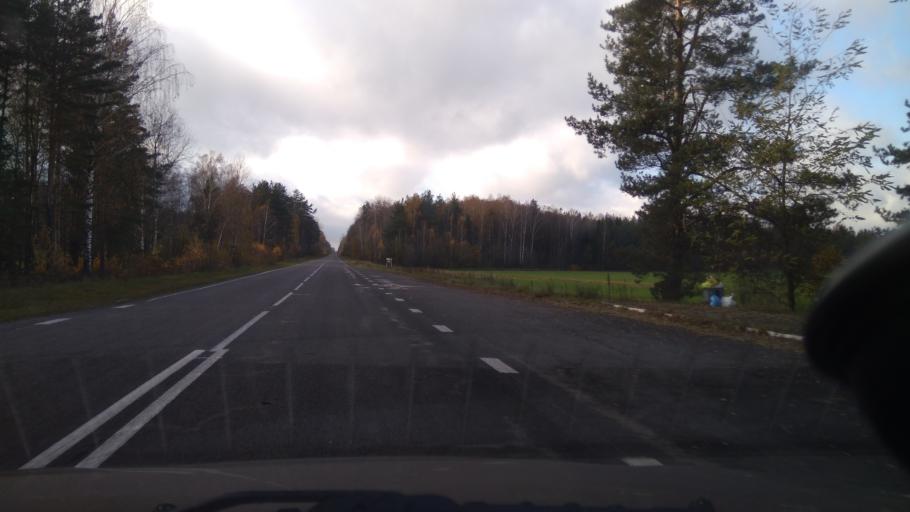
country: BY
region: Minsk
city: Urechcha
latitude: 53.2096
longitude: 27.9794
